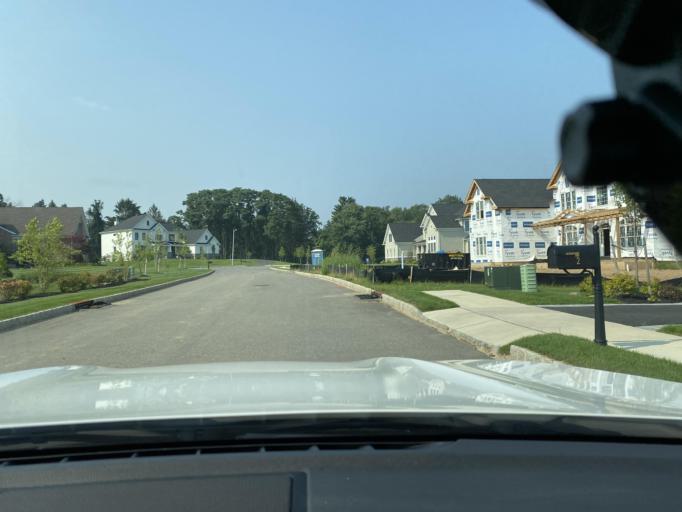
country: US
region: New York
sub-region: Rockland County
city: Airmont
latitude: 41.0778
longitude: -74.1162
